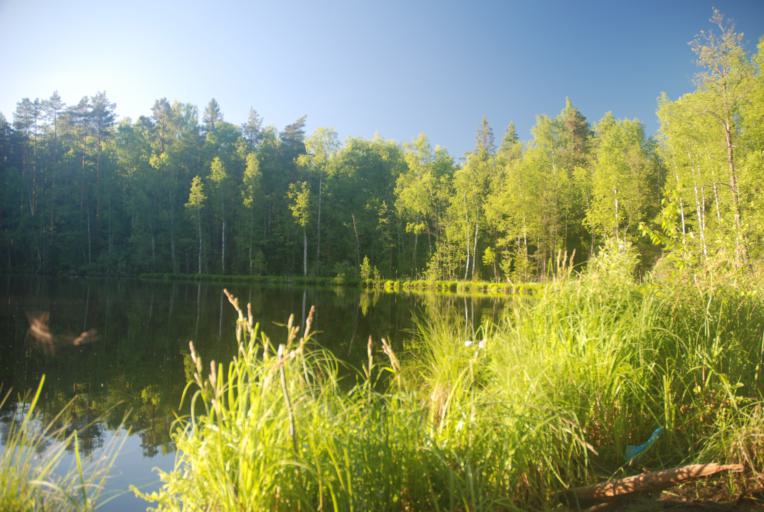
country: RU
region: Pskov
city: Strugi-Krasnyye
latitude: 57.8843
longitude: 29.1731
